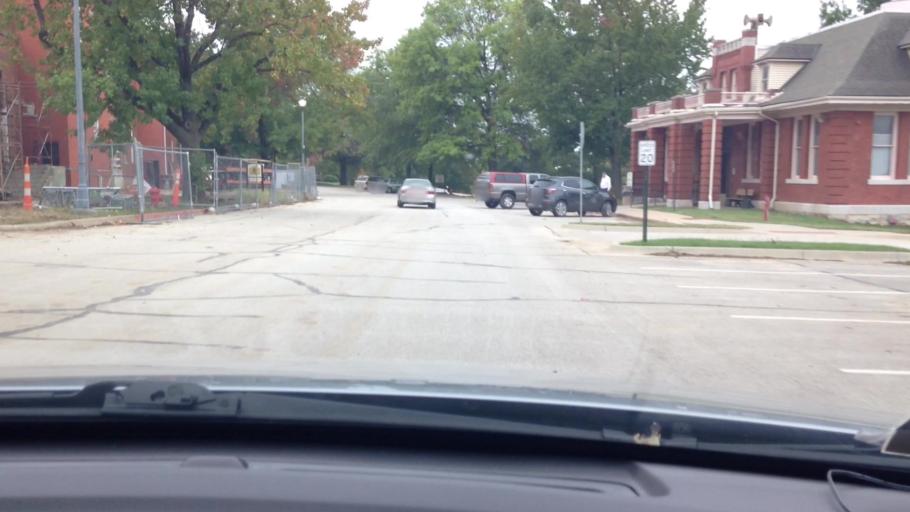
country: US
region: Kansas
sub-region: Leavenworth County
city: Lansing
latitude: 39.2793
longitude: -94.8964
